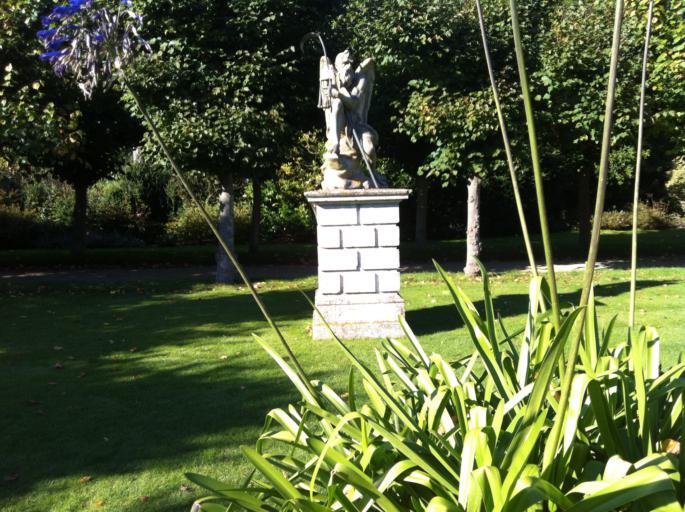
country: GB
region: England
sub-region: Norfolk
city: Dersingham
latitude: 52.8312
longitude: 0.5130
